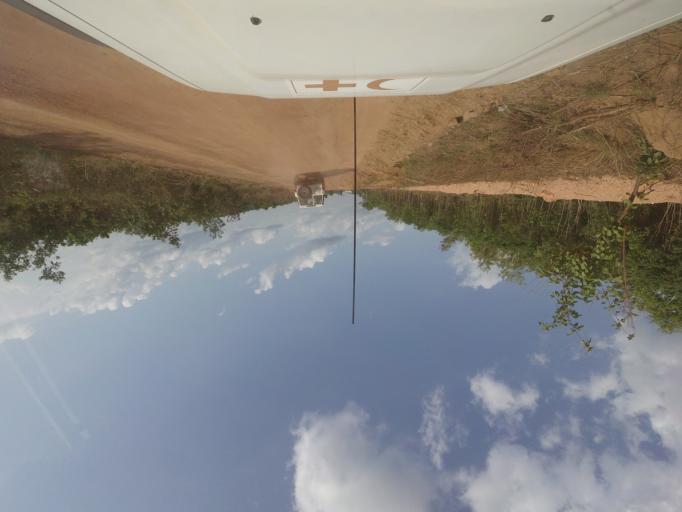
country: LR
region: Bong
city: Gbarnga
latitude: 7.0361
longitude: -9.5120
